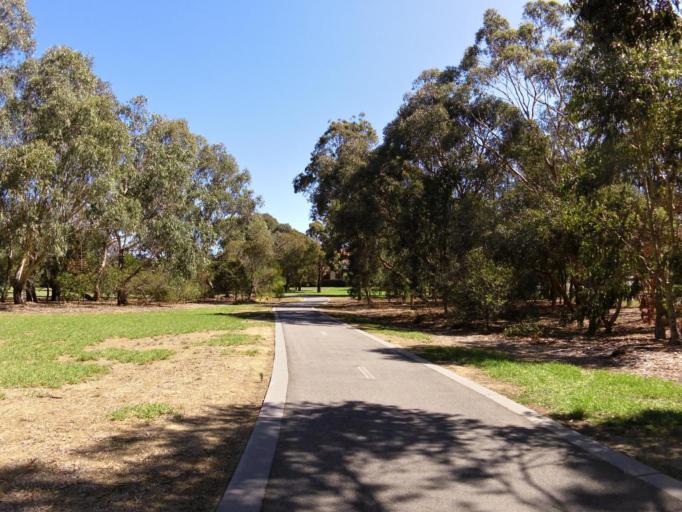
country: AU
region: Victoria
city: Alphington
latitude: -37.7916
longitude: 145.0406
